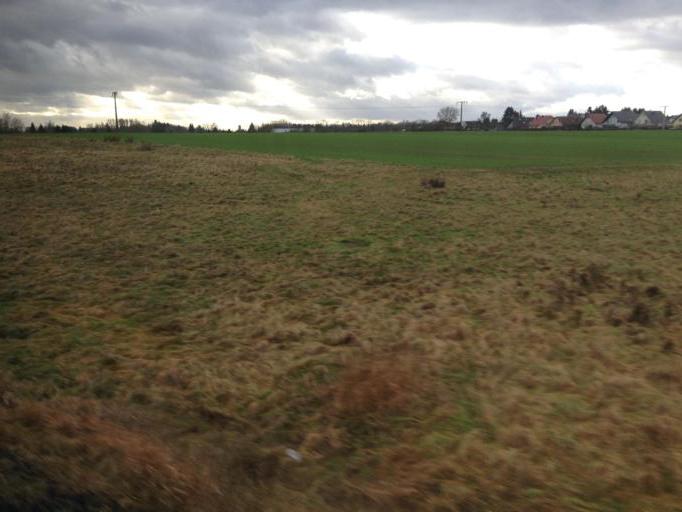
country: DE
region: Hesse
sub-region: Regierungsbezirk Giessen
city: Hungen
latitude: 50.4617
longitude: 8.9045
